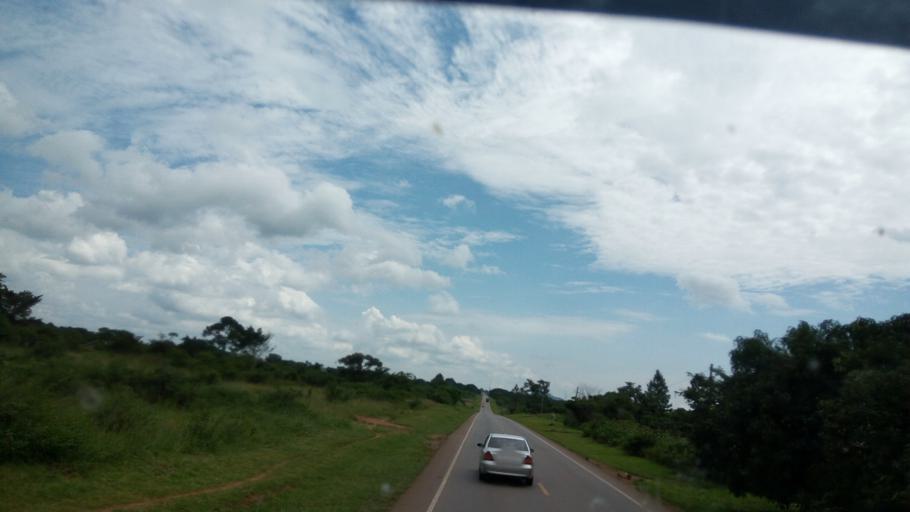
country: UG
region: Central Region
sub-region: Nakasongola District
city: Nakasongola
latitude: 1.2258
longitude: 32.4647
